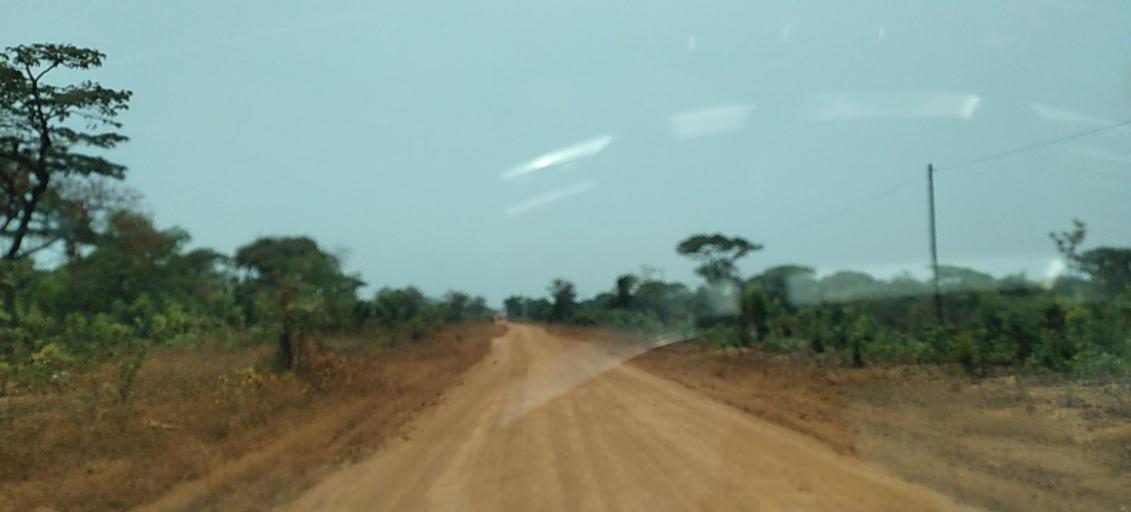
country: CD
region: Katanga
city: Kipushi
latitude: -11.9277
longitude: 26.9950
